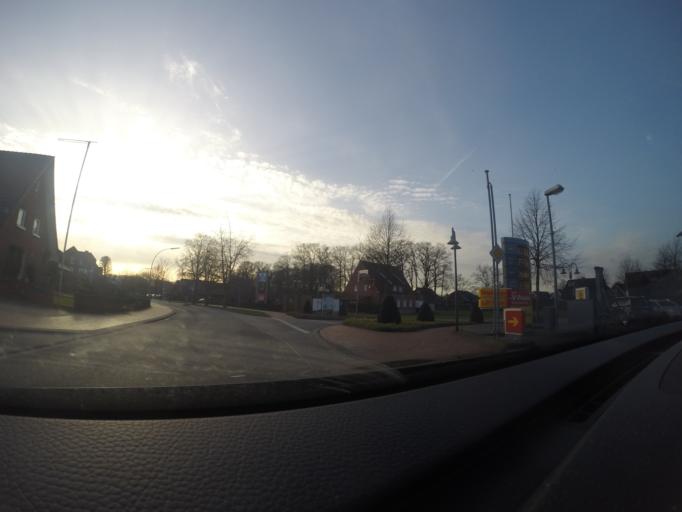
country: NL
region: Overijssel
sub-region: Gemeente Enschede
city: Enschede
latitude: 52.1272
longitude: 6.9129
